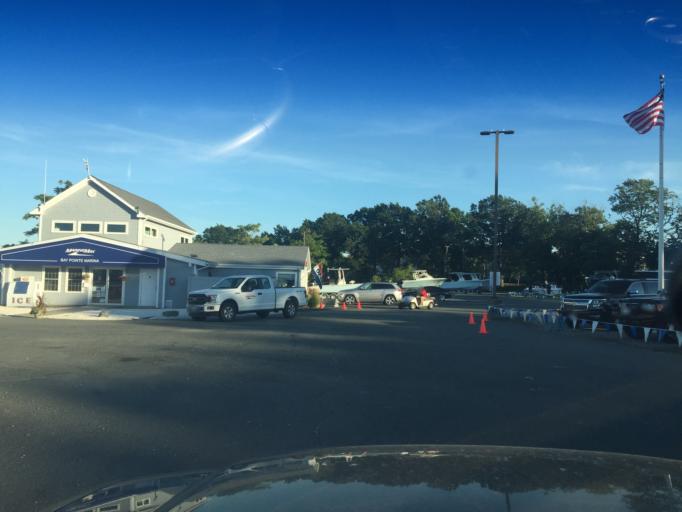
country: US
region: Massachusetts
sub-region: Norfolk County
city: Quincy
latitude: 42.2495
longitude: -70.9748
